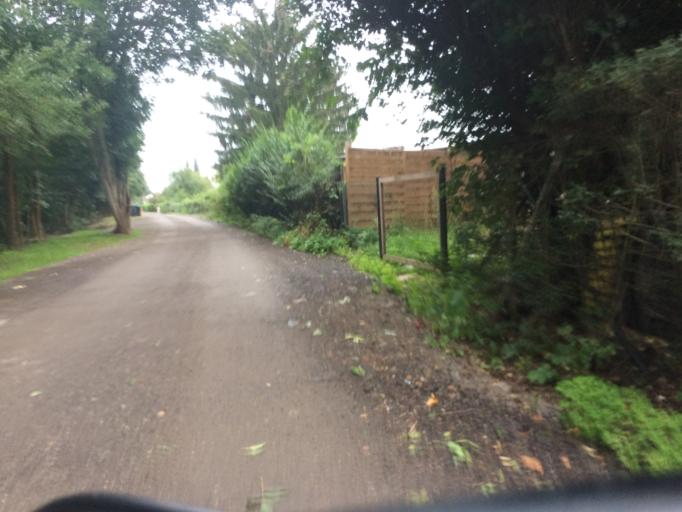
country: DE
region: Berlin
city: Buchholz
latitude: 52.6012
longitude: 13.4152
